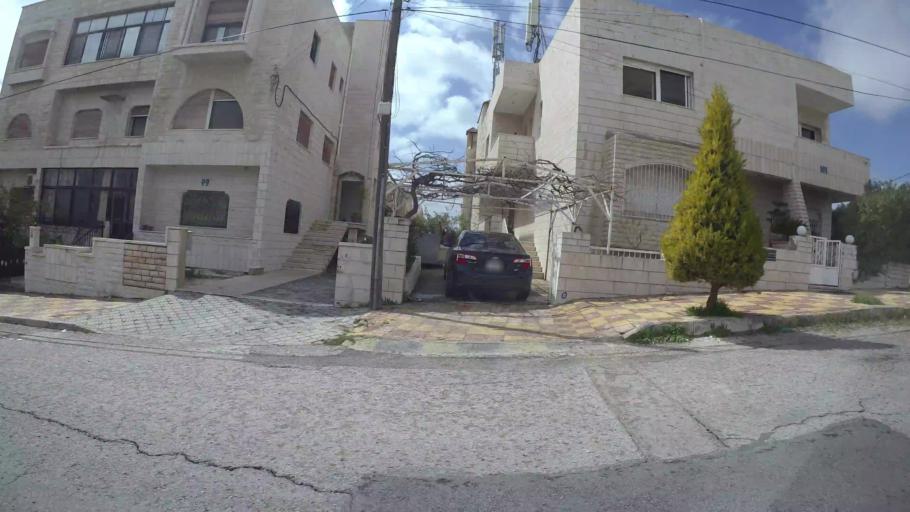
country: JO
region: Amman
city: Al Jubayhah
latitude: 31.9909
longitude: 35.8529
